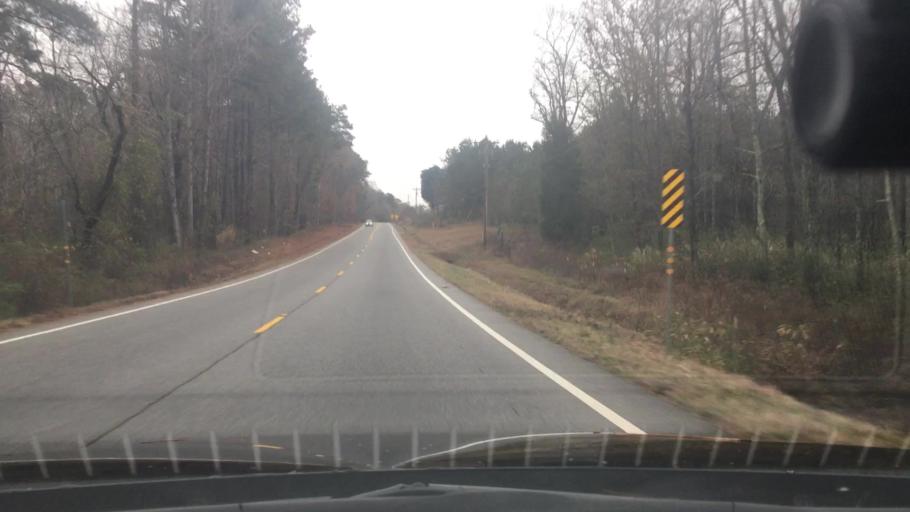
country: US
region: Georgia
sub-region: Spalding County
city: Experiment
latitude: 33.2406
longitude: -84.4179
